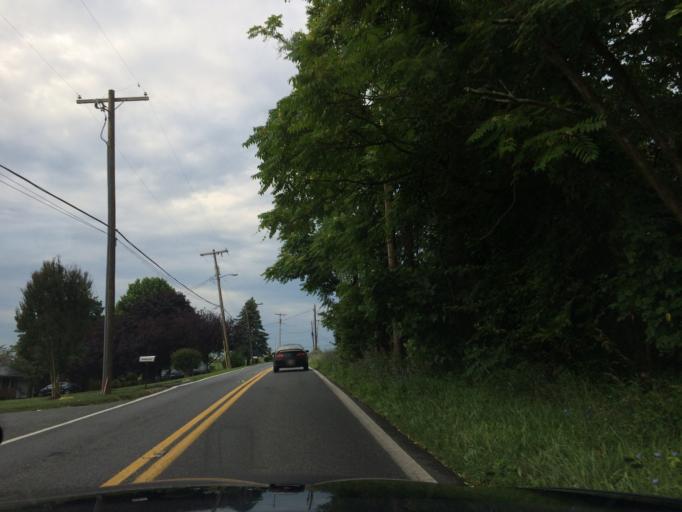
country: US
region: Maryland
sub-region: Montgomery County
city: Clarksburg
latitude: 39.2509
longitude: -77.2760
